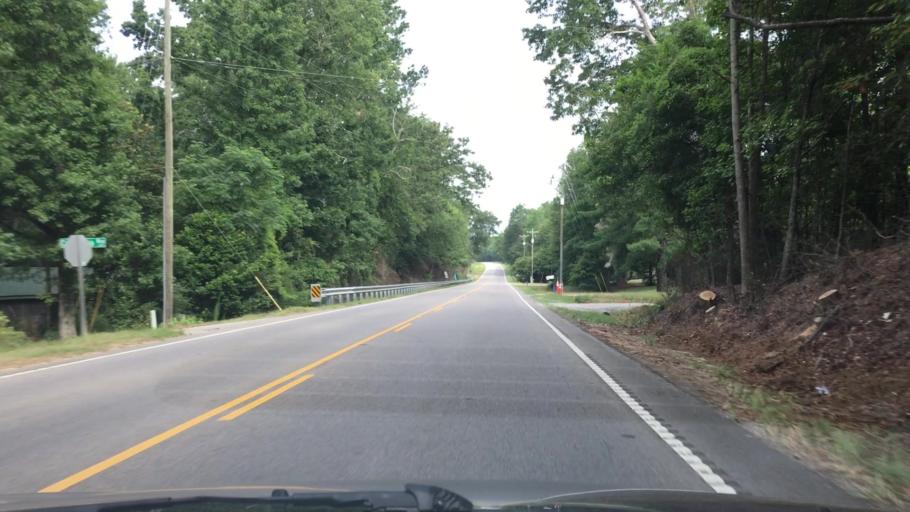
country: US
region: South Carolina
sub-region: Barnwell County
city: Williston
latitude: 33.6552
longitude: -81.3737
